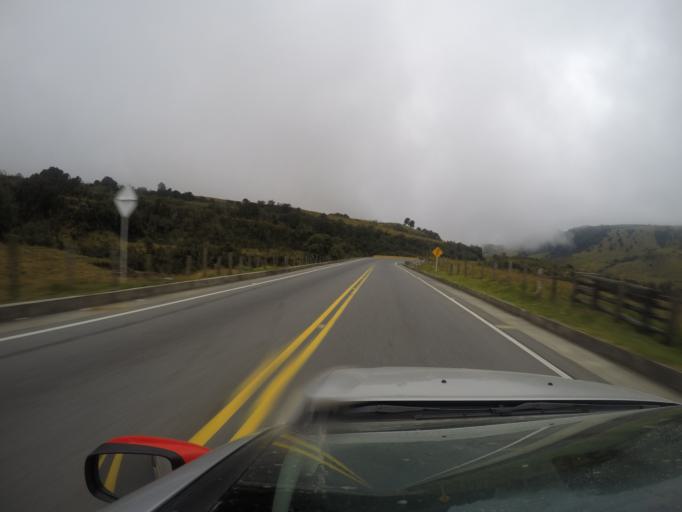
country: CO
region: Tolima
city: Herveo
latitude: 5.0536
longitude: -75.3246
